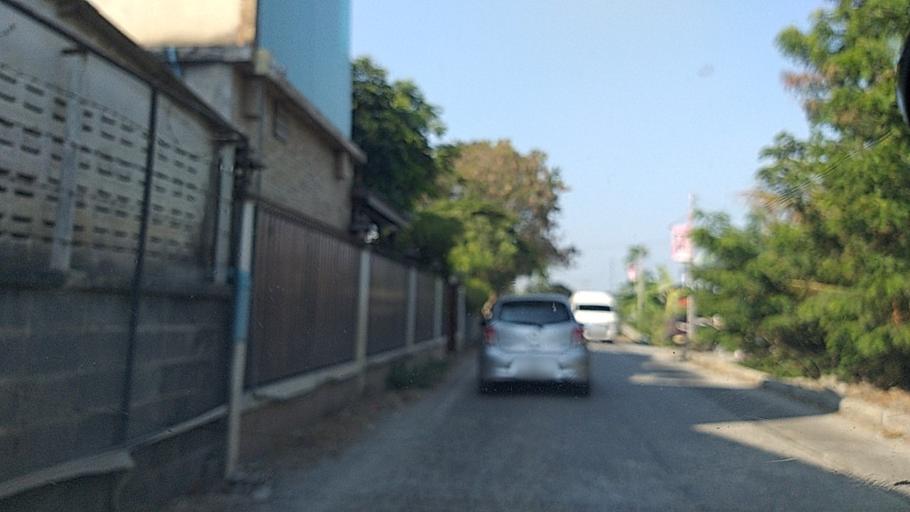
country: TH
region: Nonthaburi
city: Bang Bua Thong
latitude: 13.9342
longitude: 100.3790
